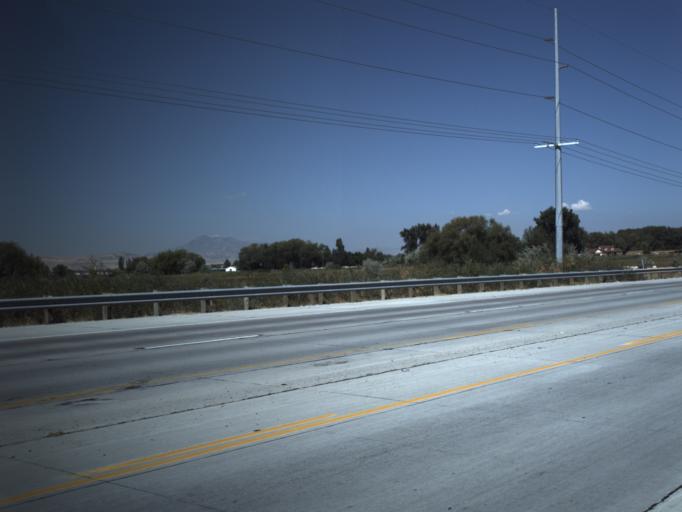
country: US
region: Utah
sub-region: Cache County
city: Logan
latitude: 41.7081
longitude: -111.8604
